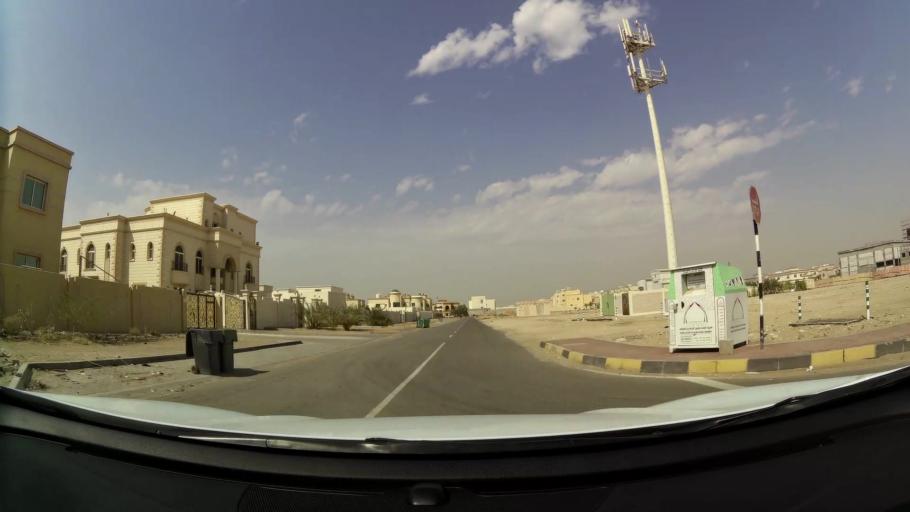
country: AE
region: Abu Dhabi
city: Abu Dhabi
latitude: 24.3295
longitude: 54.5461
